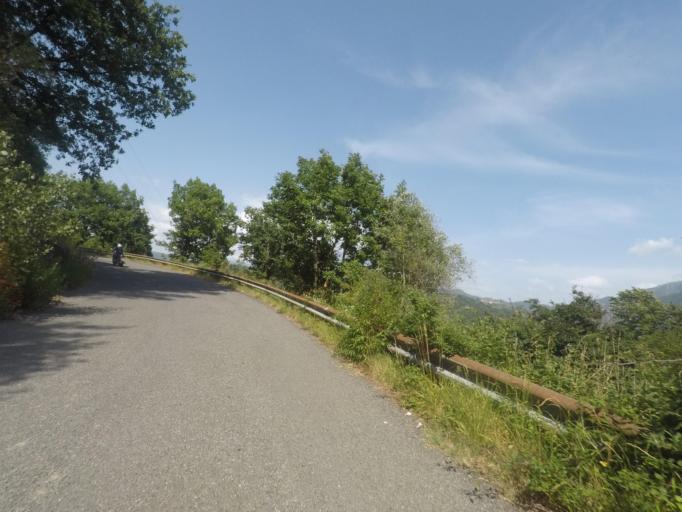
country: IT
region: Tuscany
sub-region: Provincia di Massa-Carrara
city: Fivizzano
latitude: 44.1700
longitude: 10.1079
